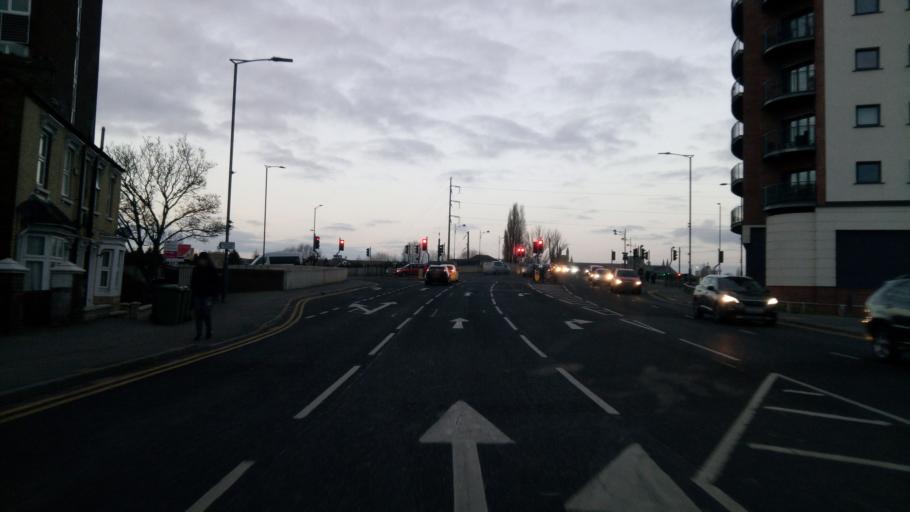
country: GB
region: England
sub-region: Peterborough
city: Peterborough
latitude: 52.5656
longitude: -0.2422
